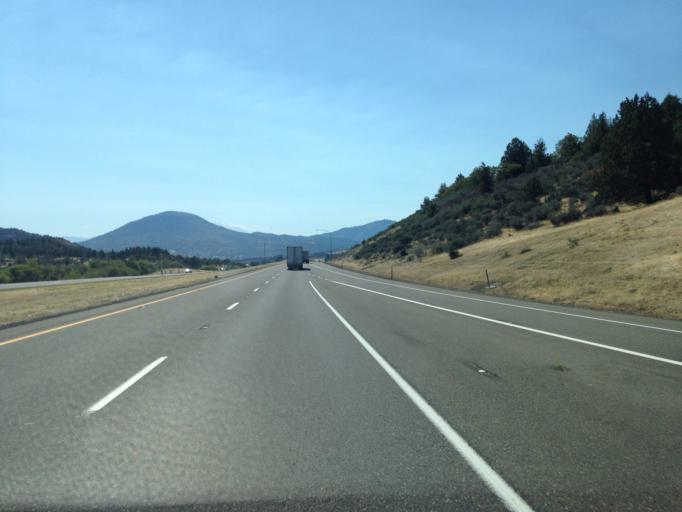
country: US
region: California
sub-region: Siskiyou County
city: Yreka
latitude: 41.9518
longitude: -122.5906
